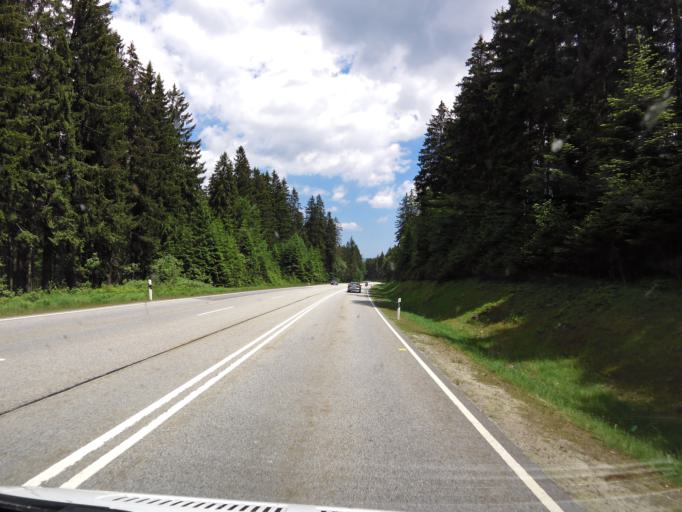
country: DE
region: Bavaria
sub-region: Lower Bavaria
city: Philippsreut
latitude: 48.8735
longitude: 13.6883
